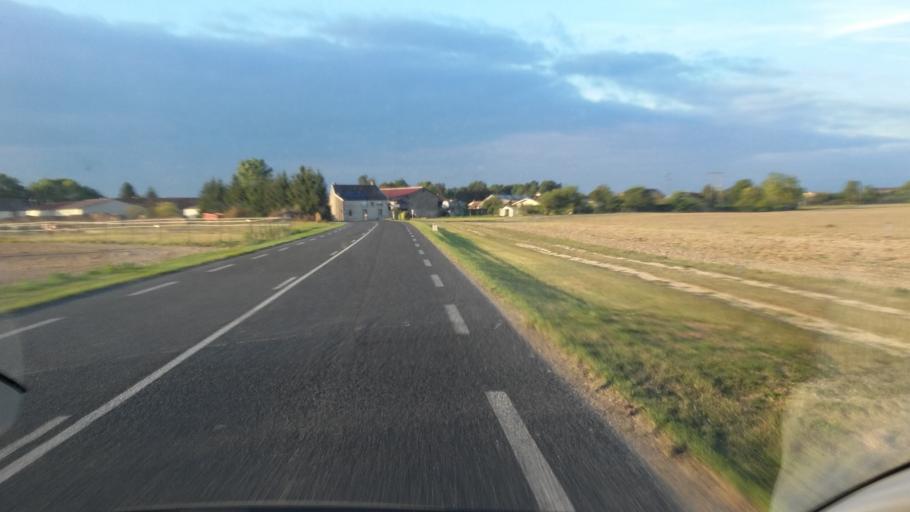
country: FR
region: Champagne-Ardenne
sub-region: Departement de la Marne
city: Fere-Champenoise
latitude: 48.8098
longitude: 3.9927
